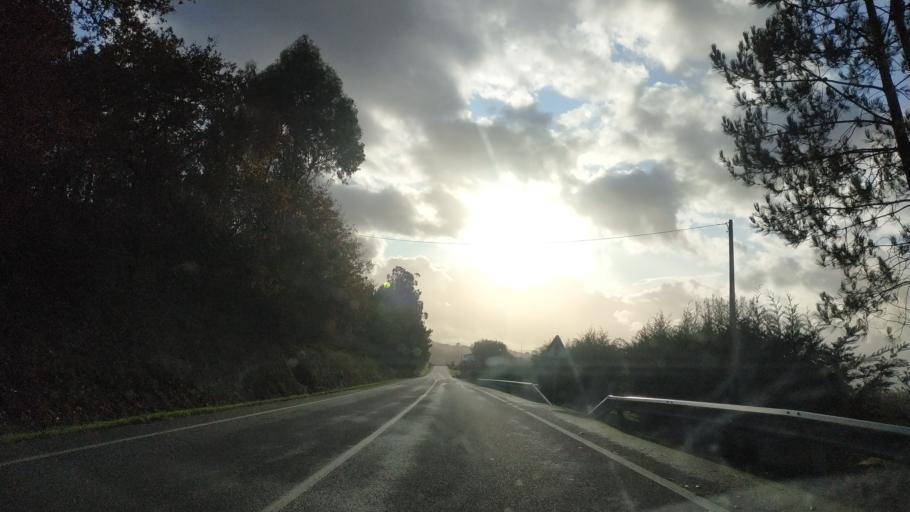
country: ES
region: Galicia
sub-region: Provincia de Pontevedra
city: Silleda
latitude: 42.7875
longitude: -8.1667
